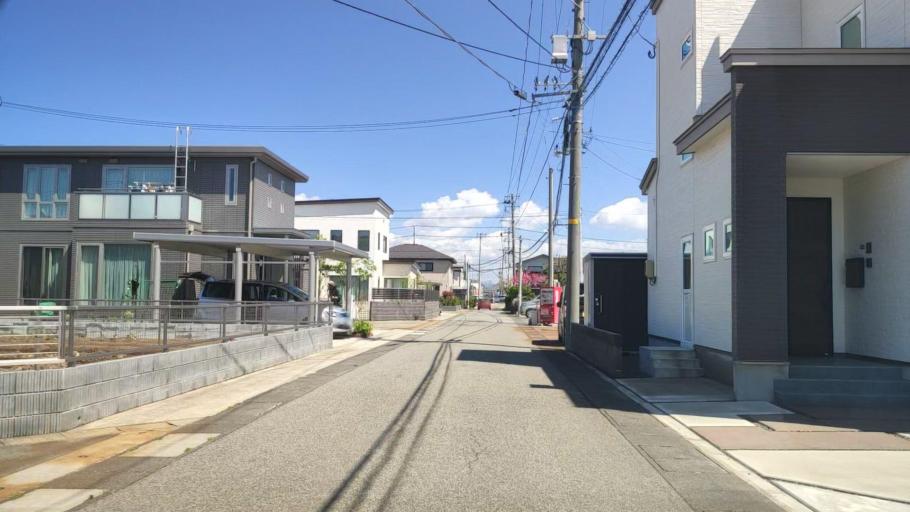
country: JP
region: Akita
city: Omagari
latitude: 39.4671
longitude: 140.4830
